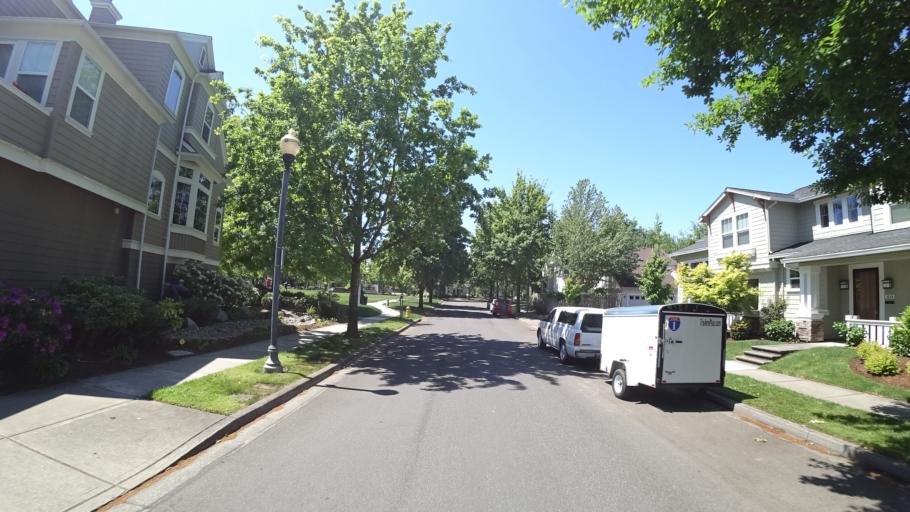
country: US
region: Oregon
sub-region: Washington County
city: Rockcreek
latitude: 45.5372
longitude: -122.9126
